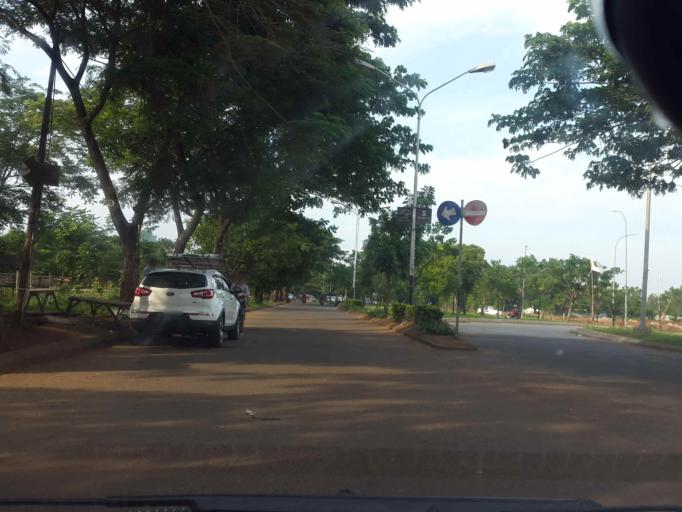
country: ID
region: West Java
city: Ciputat
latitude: -6.2681
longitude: 106.6882
